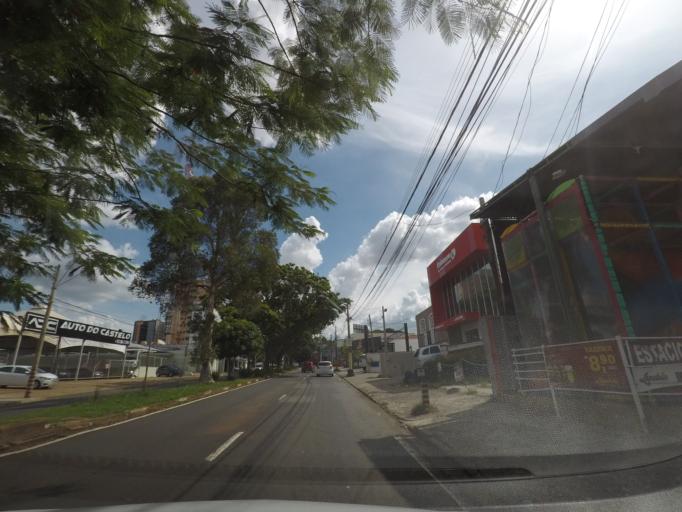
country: BR
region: Sao Paulo
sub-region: Campinas
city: Campinas
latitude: -22.8878
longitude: -47.0762
